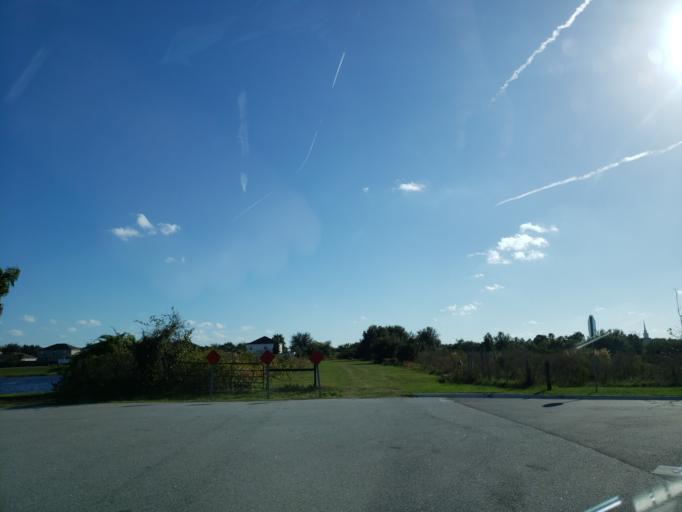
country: US
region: Florida
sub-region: Hillsborough County
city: Balm
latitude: 27.7902
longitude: -82.3287
